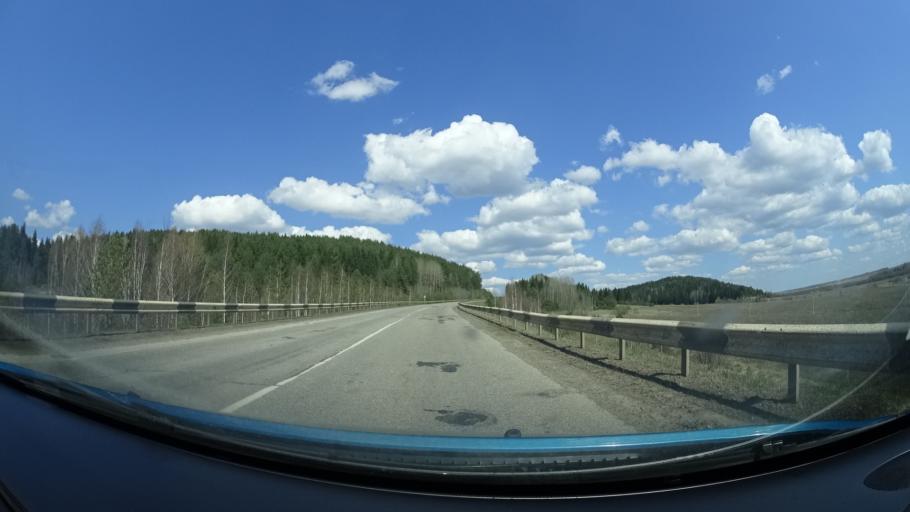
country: RU
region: Perm
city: Osa
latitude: 57.3025
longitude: 55.6163
